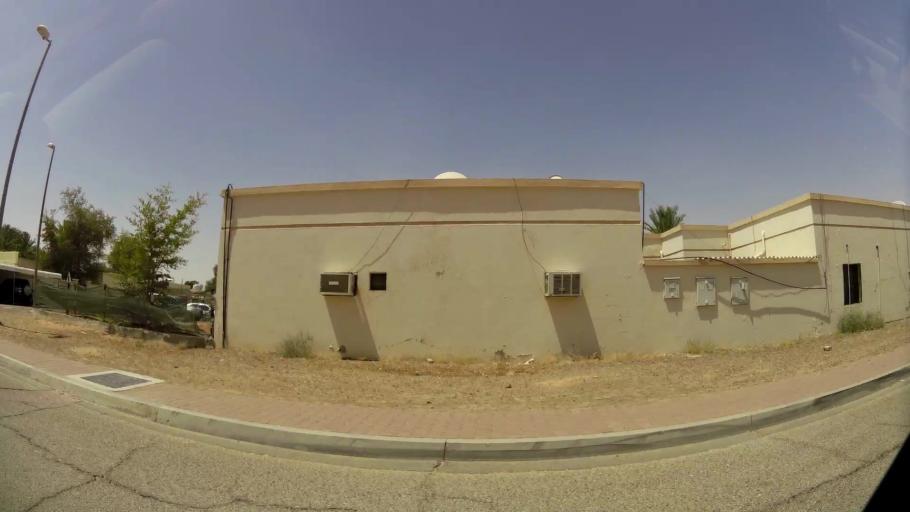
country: OM
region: Al Buraimi
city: Al Buraymi
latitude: 24.2866
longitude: 55.7647
